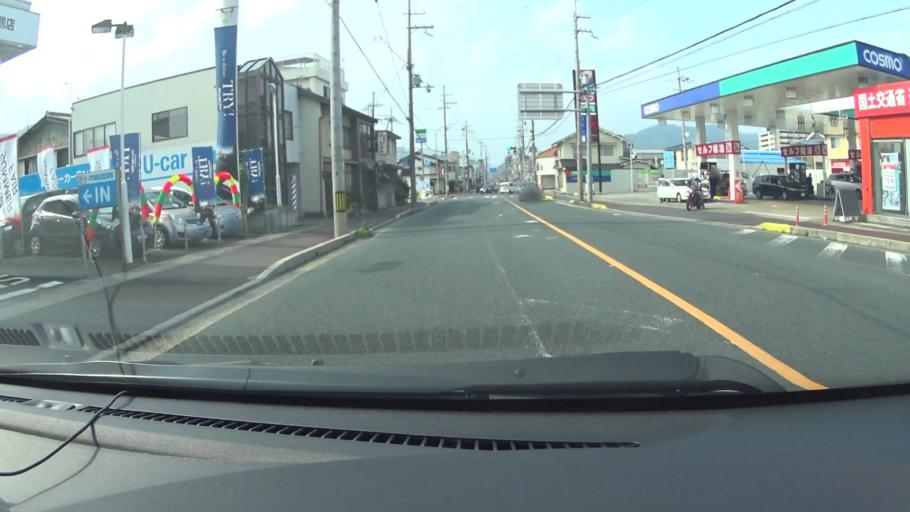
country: JP
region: Kyoto
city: Maizuru
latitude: 35.4361
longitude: 135.3284
